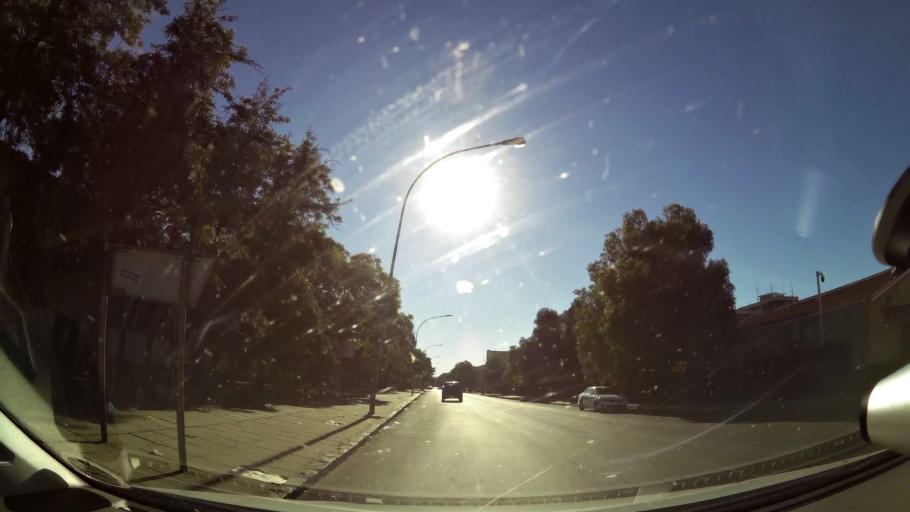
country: ZA
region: Northern Cape
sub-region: Frances Baard District Municipality
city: Kimberley
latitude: -28.7461
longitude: 24.7701
